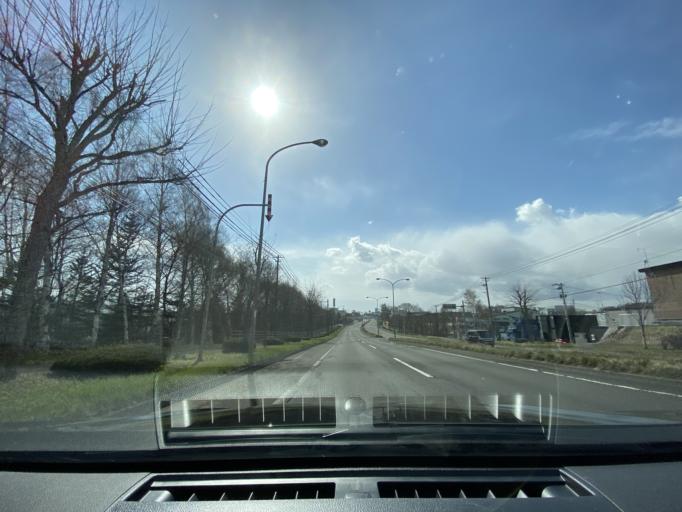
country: JP
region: Hokkaido
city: Kitahiroshima
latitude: 42.9689
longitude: 141.4817
